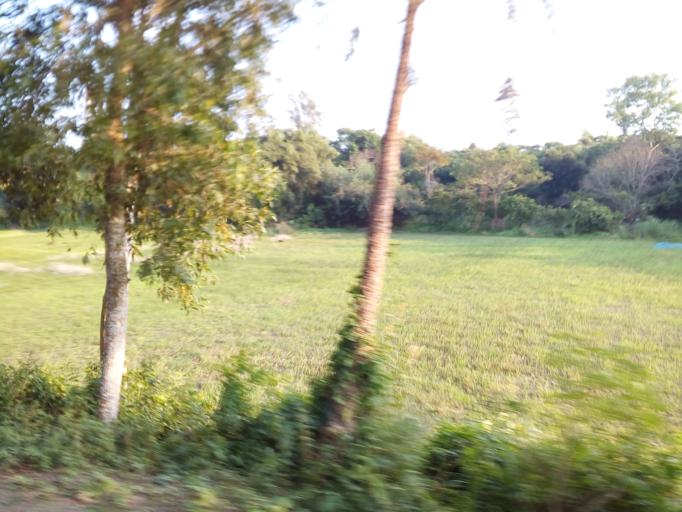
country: BD
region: Dhaka
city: Nagarpur
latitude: 23.8528
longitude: 89.9107
